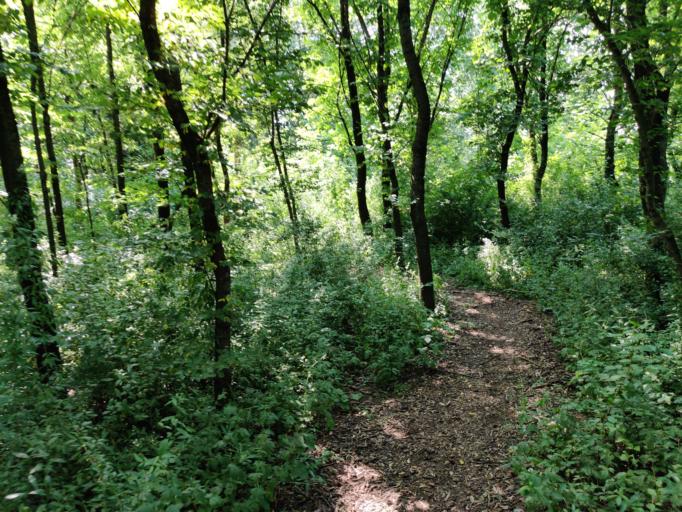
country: HU
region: Hajdu-Bihar
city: Balmazujvaros
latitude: 47.6121
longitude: 21.3275
